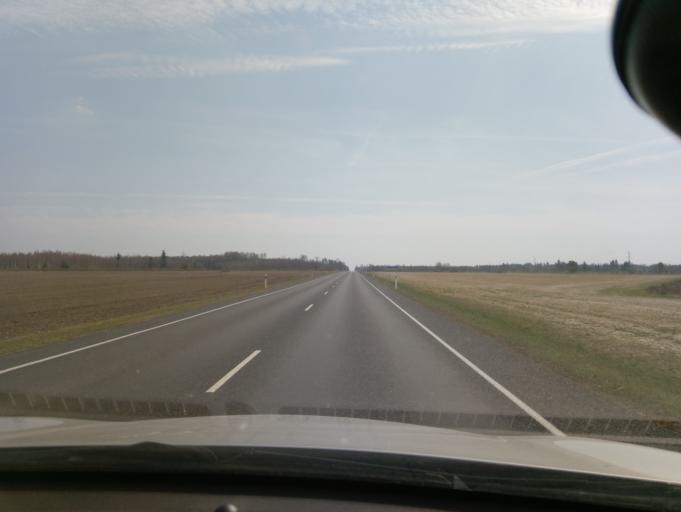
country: EE
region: Viljandimaa
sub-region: Vohma linn
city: Vohma
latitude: 58.7327
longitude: 25.5921
